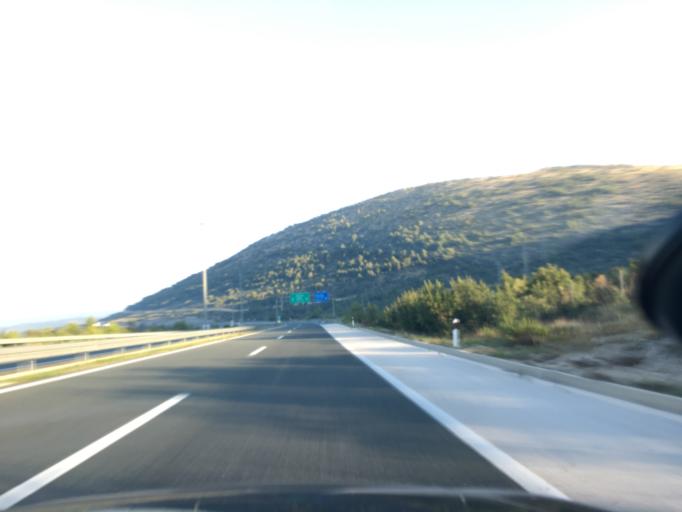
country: HR
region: Sibensko-Kniniska
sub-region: Grad Sibenik
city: Sibenik
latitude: 43.7644
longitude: 15.9342
